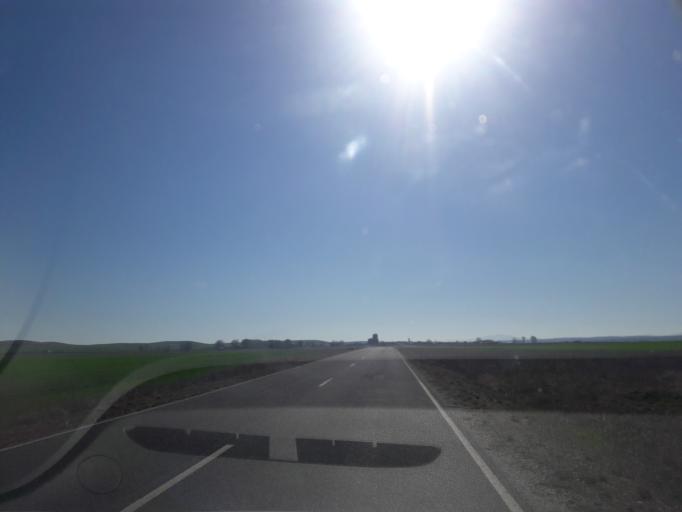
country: ES
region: Castille and Leon
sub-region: Provincia de Salamanca
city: Salmoral
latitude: 40.8073
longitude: -5.2350
